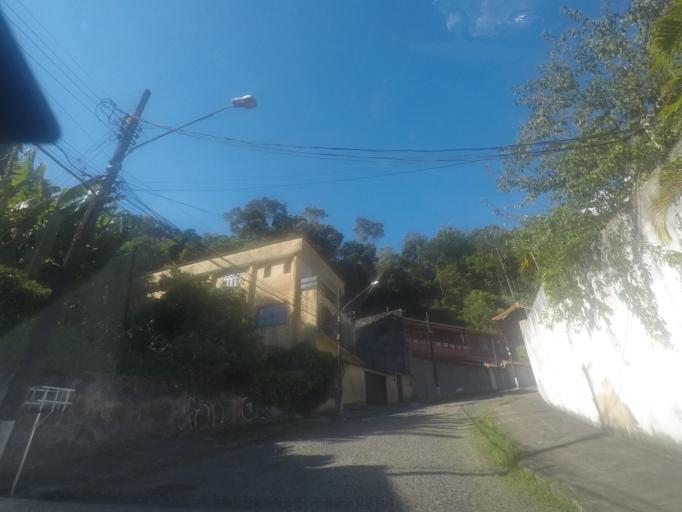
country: BR
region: Rio de Janeiro
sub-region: Petropolis
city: Petropolis
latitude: -22.5140
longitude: -43.1708
